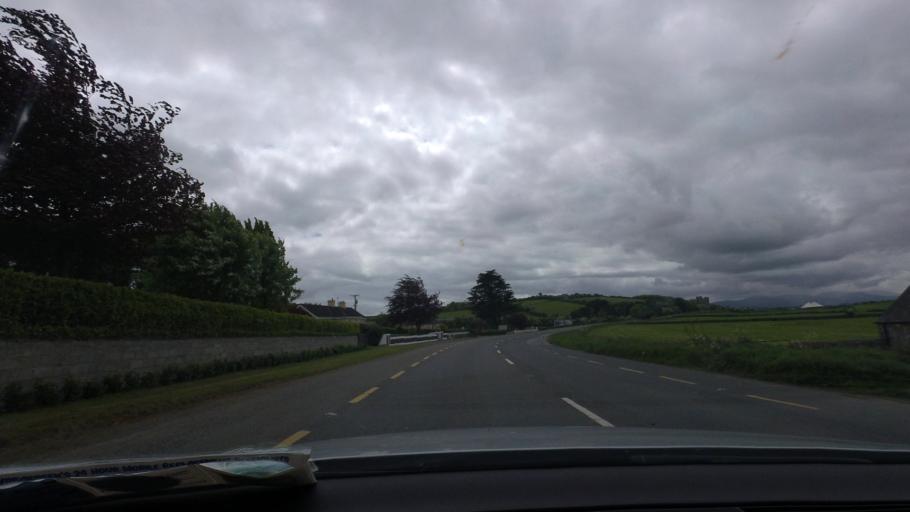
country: IE
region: Munster
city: Cashel
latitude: 52.5307
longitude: -7.8782
